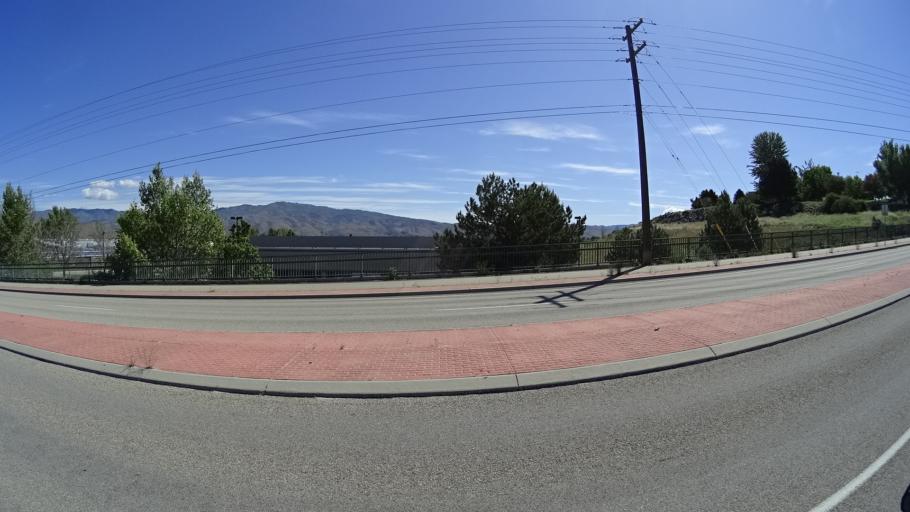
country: US
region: Idaho
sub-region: Ada County
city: Boise
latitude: 43.5464
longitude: -116.1585
